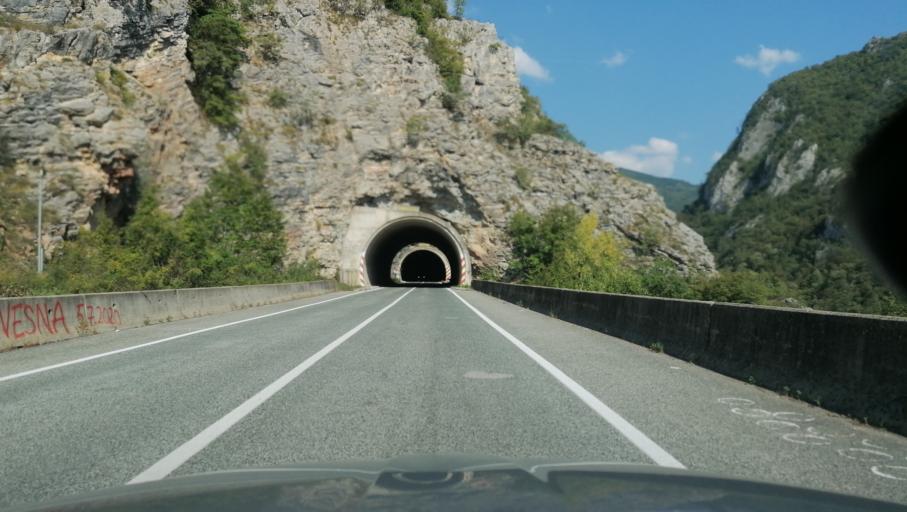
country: BA
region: Republika Srpska
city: Visegrad
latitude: 43.7326
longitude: 19.1892
